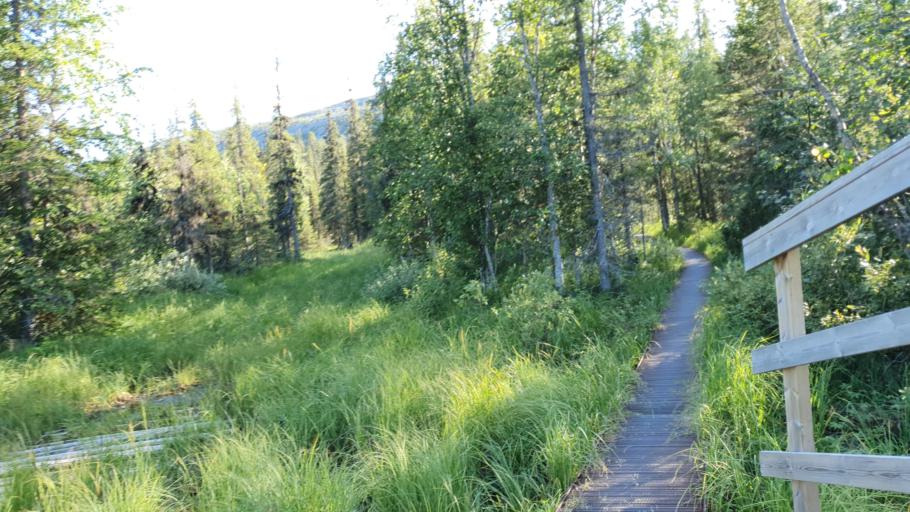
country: FI
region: Lapland
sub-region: Tunturi-Lappi
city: Kolari
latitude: 67.5977
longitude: 24.2553
